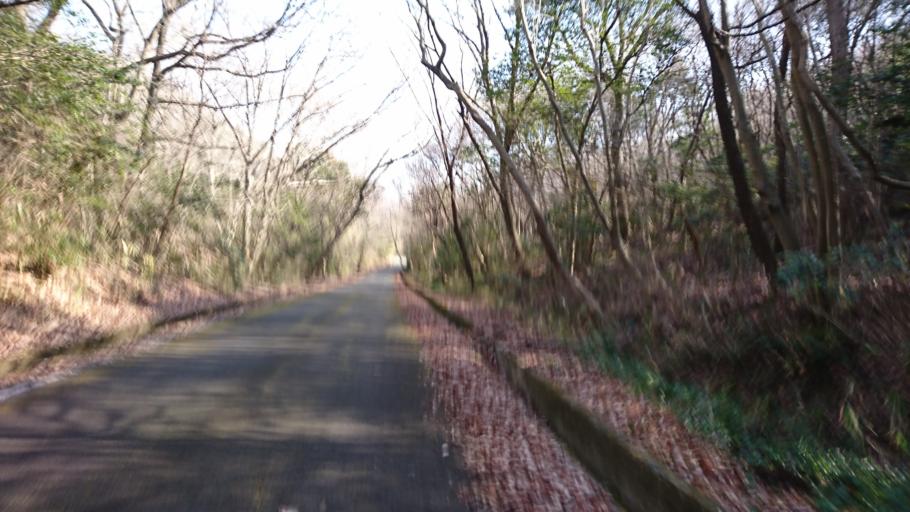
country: JP
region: Hyogo
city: Kakogawacho-honmachi
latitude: 34.8241
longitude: 134.8649
